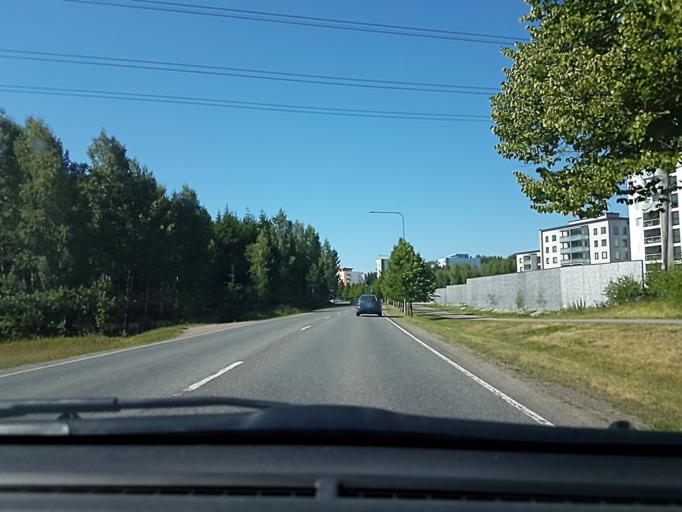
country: FI
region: Uusimaa
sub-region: Helsinki
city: Vantaa
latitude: 60.3370
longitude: 25.0674
